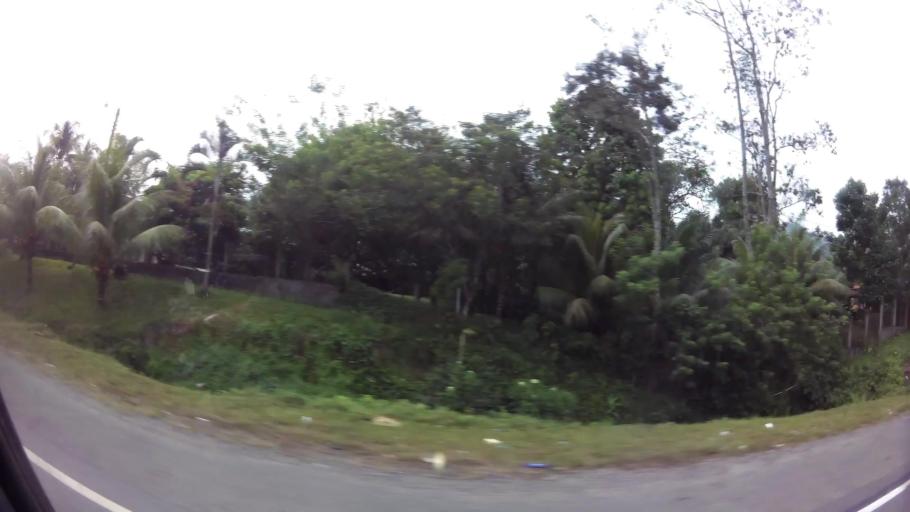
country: HN
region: Yoro
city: Toyos
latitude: 15.5215
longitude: -87.6606
